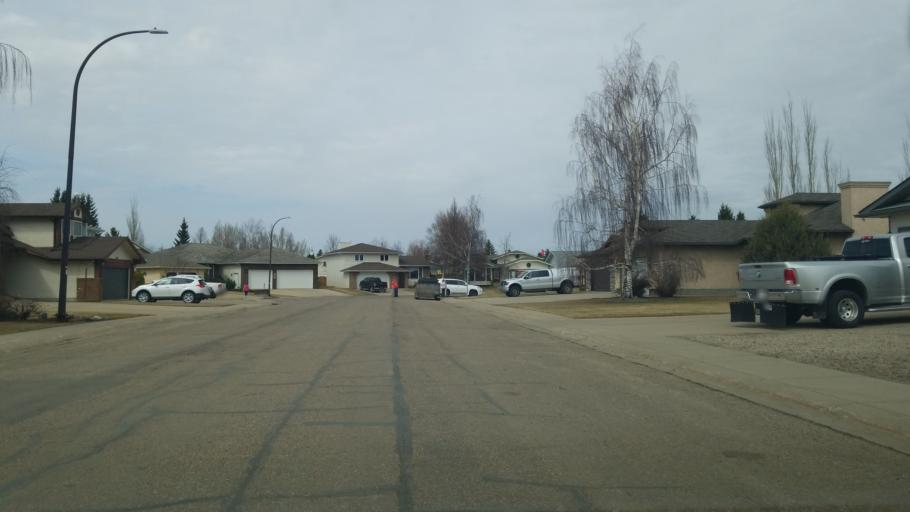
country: CA
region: Saskatchewan
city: Lloydminster
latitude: 53.2721
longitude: -110.0289
